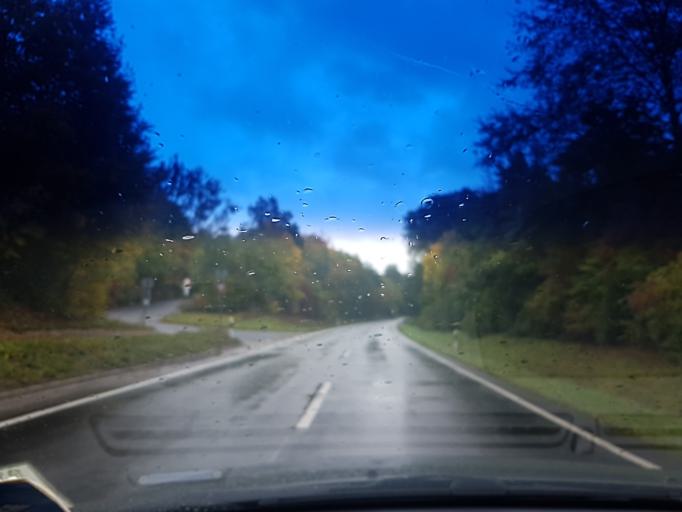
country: DE
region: Bavaria
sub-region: Upper Franconia
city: Bischberg
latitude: 49.9320
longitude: 10.8453
